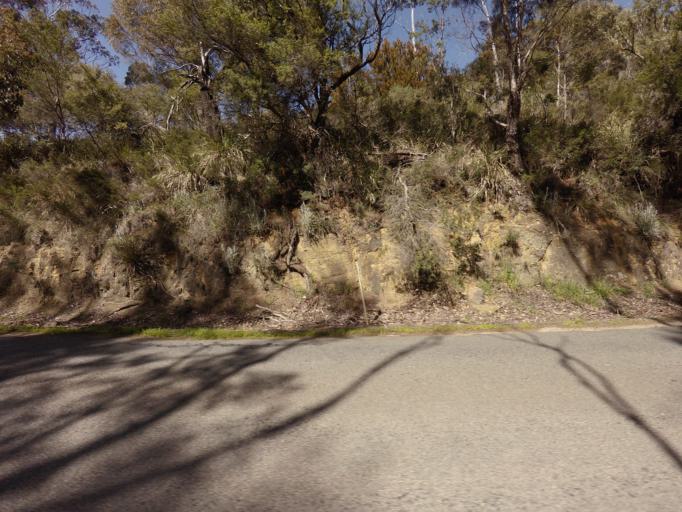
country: AU
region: Tasmania
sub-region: Derwent Valley
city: New Norfolk
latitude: -42.6816
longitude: 146.7456
